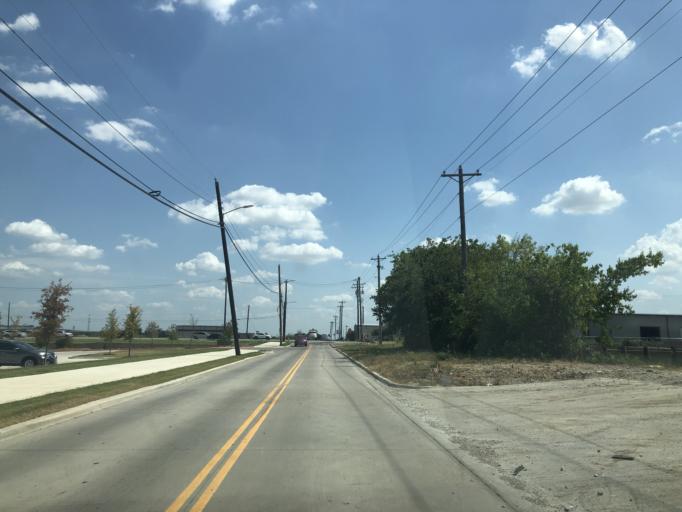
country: US
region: Texas
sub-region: Tarrant County
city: Haslet
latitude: 32.9347
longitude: -97.3228
